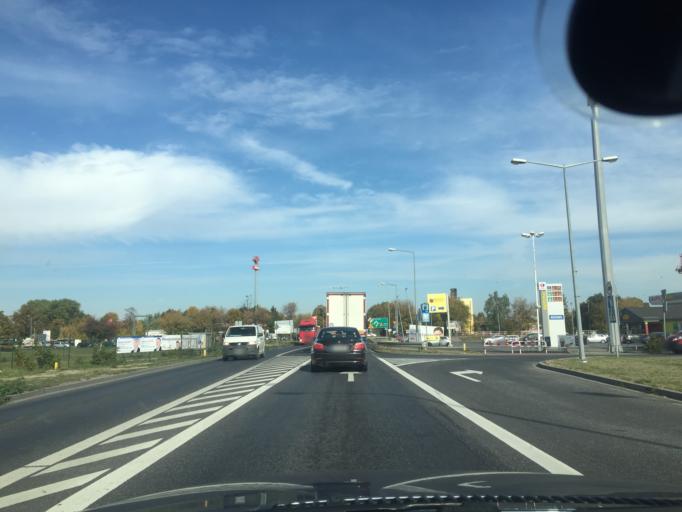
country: PL
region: Greater Poland Voivodeship
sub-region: Powiat wrzesinski
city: Wrzesnia
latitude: 52.3125
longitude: 17.5537
